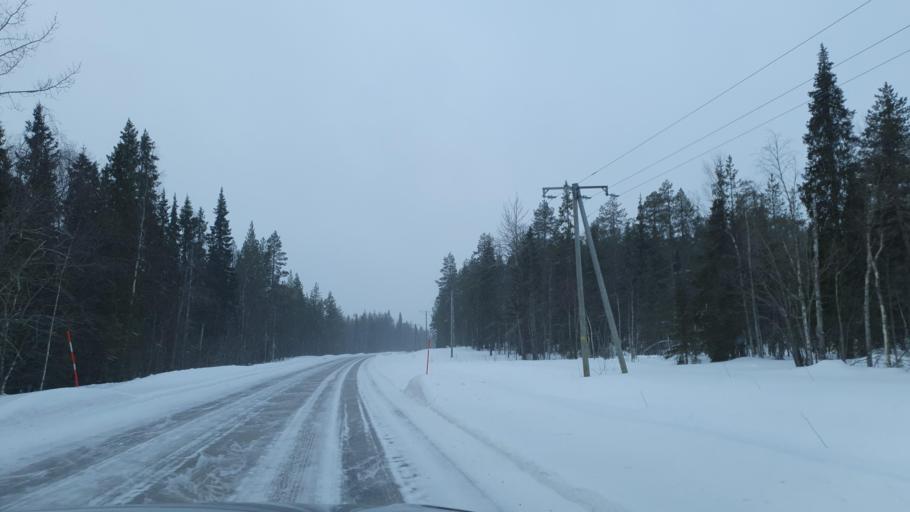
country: FI
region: Lapland
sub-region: Tunturi-Lappi
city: Kolari
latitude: 67.4454
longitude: 23.8425
